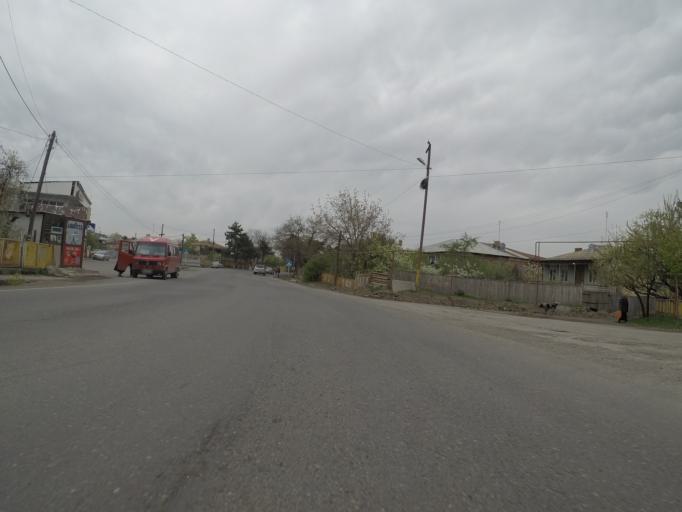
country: GE
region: Shida Kartli
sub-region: Khashuris Raioni
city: Khashuri
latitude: 41.9886
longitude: 43.6036
